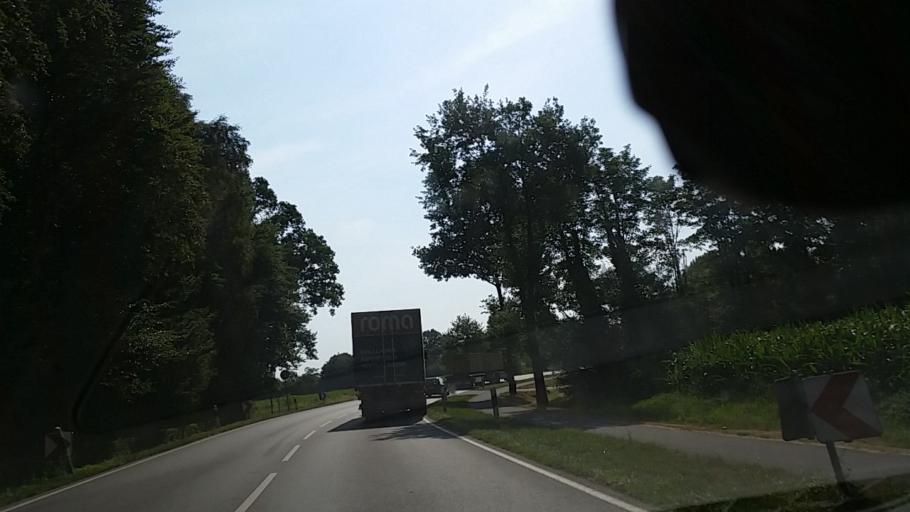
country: DE
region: Lower Saxony
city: Steinfeld
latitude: 52.5947
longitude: 8.1867
